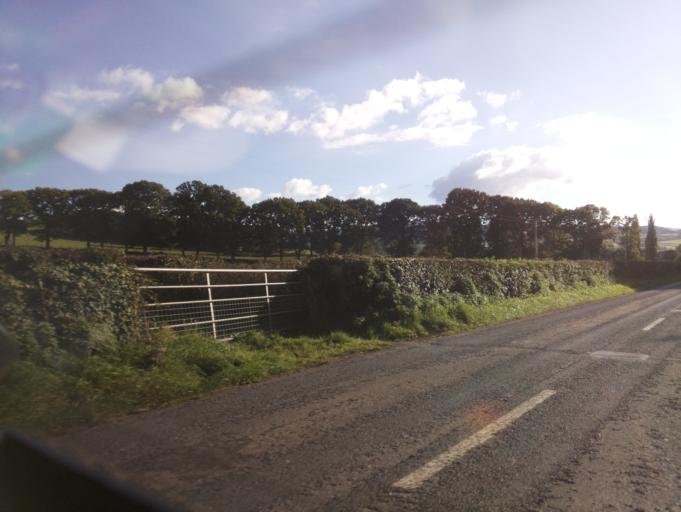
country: GB
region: Wales
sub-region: Sir Powys
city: Hay
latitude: 52.0833
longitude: -3.1192
